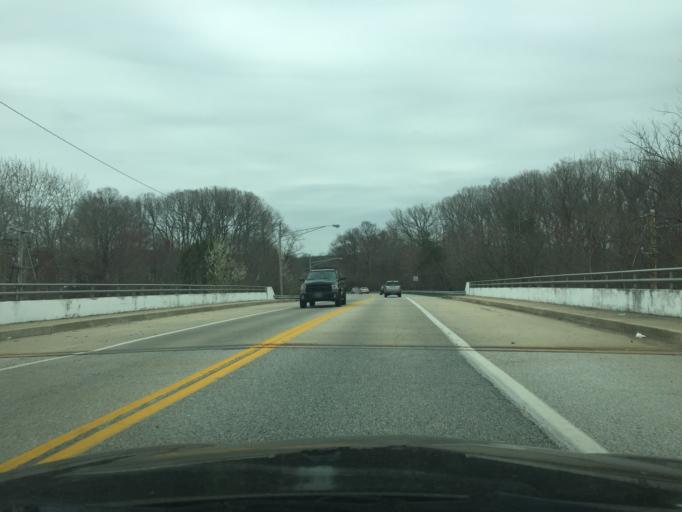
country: US
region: Maryland
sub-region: Baltimore County
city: Bowleys Quarters
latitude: 39.3637
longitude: -76.3665
